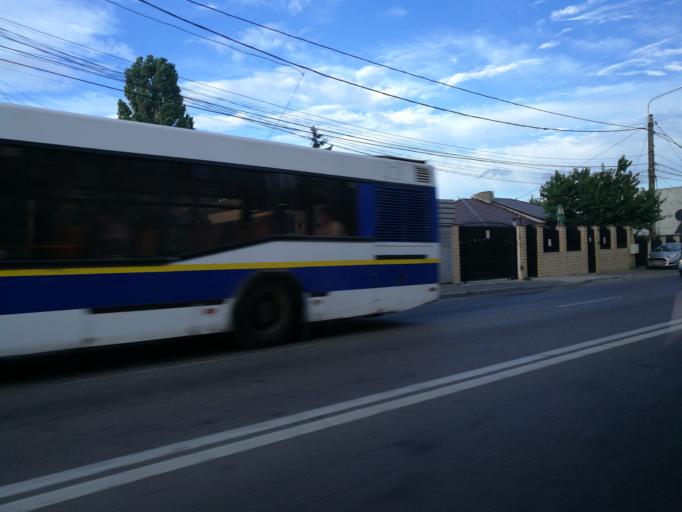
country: RO
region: Constanta
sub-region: Municipiul Constanta
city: Constanta
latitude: 44.1527
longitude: 28.6211
